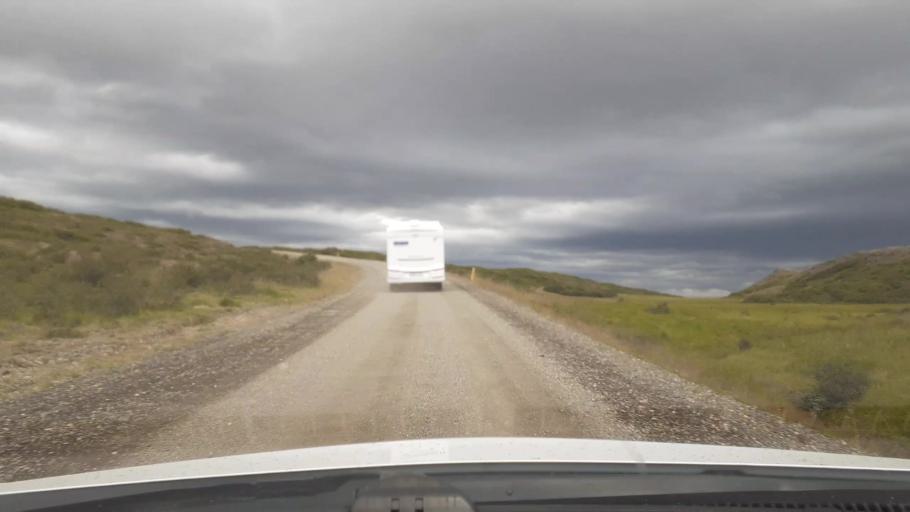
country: IS
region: West
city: Borgarnes
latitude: 64.5563
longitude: -21.6235
